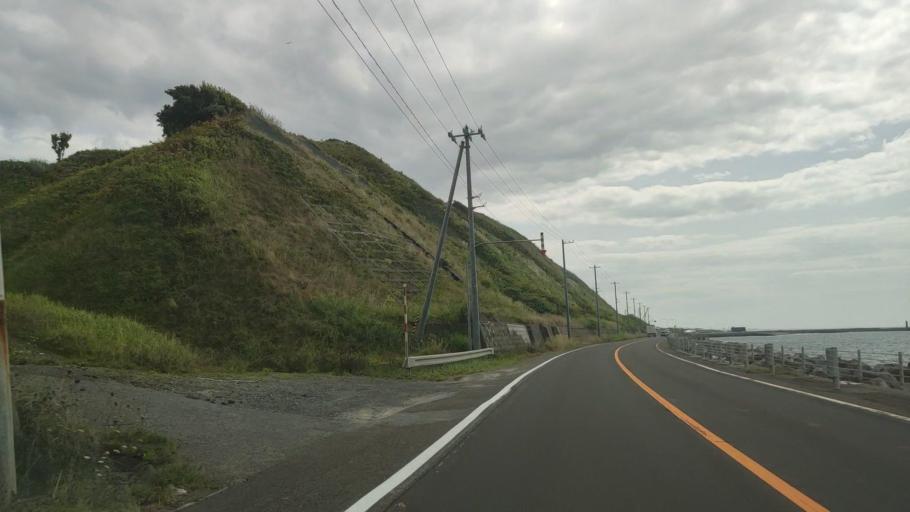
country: JP
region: Hokkaido
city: Rumoi
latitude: 44.5434
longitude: 141.7667
